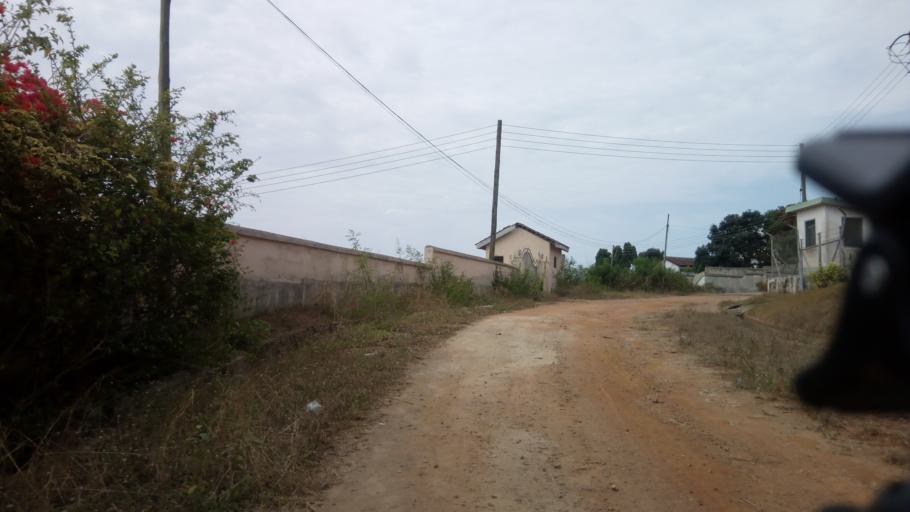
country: GH
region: Central
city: Cape Coast
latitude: 5.1041
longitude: -1.2695
